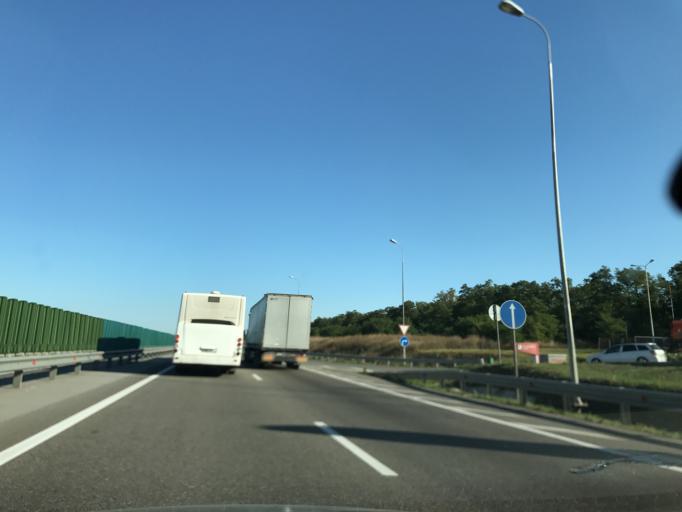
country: RU
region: Rostov
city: Tarasovskiy
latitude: 48.6452
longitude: 40.3577
